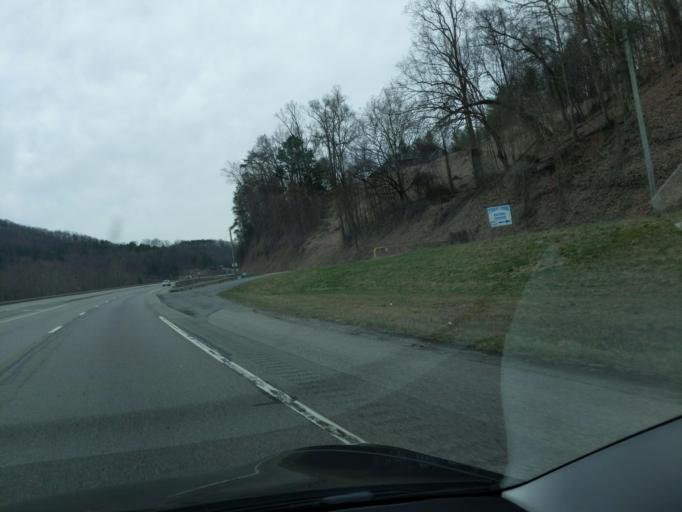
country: US
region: Kentucky
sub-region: Knox County
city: Barbourville
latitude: 36.8640
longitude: -83.7977
